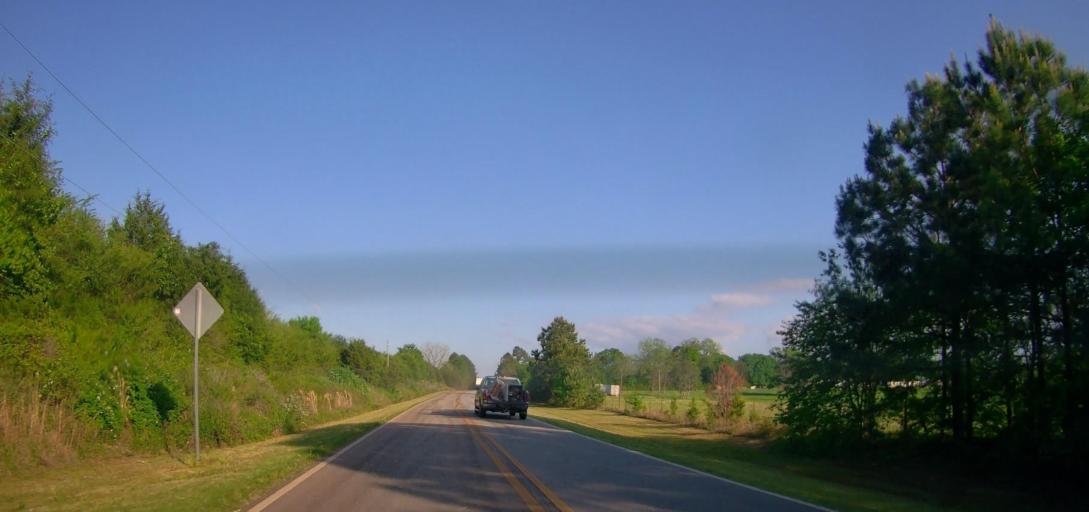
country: US
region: Georgia
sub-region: Putnam County
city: Eatonton
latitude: 33.3115
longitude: -83.3581
